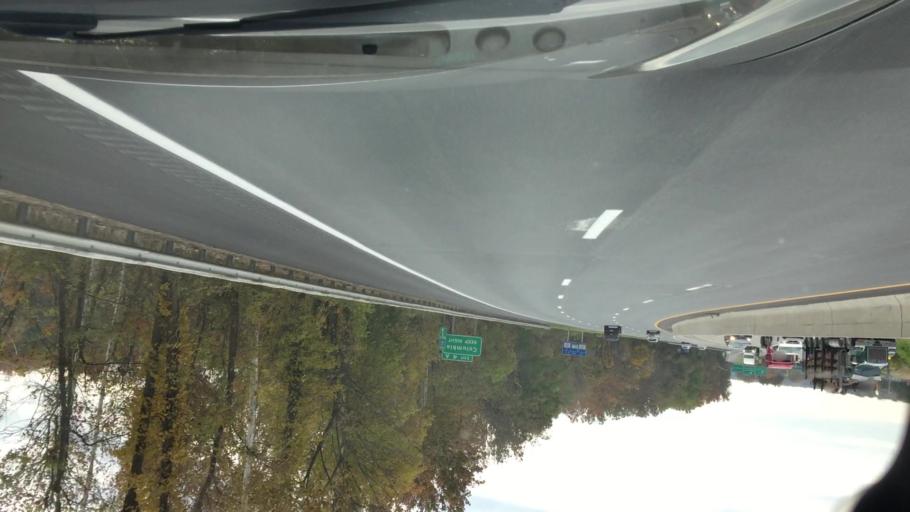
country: US
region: Pennsylvania
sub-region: Northampton County
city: East Bangor
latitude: 40.9347
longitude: -75.1031
